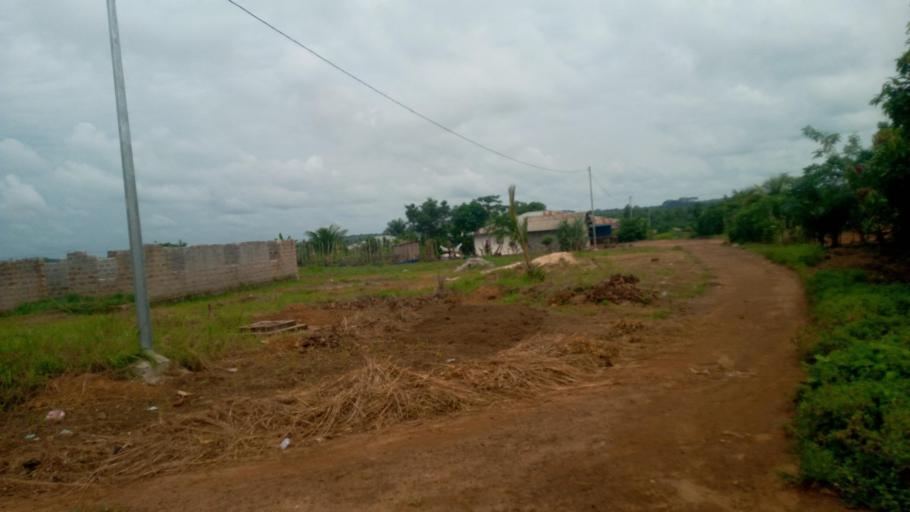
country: SL
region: Southern Province
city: Mogbwemo
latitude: 7.7771
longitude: -12.3011
